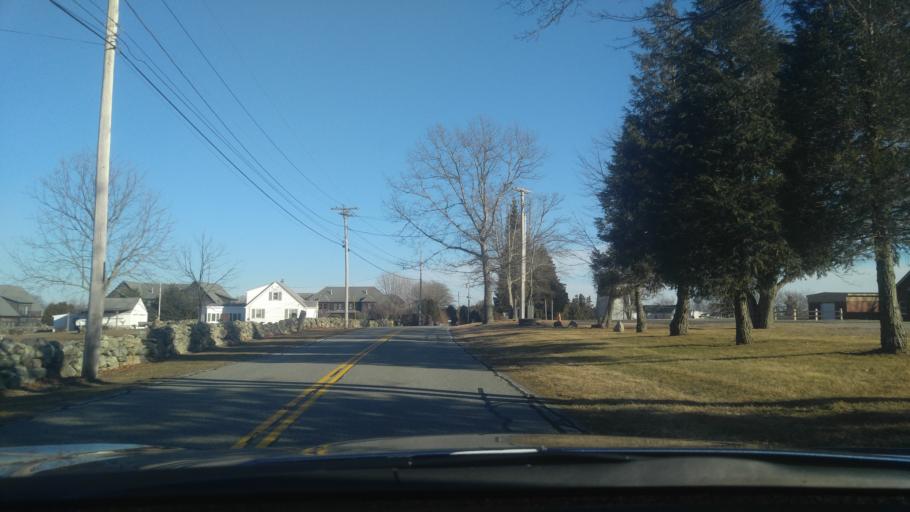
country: US
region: Rhode Island
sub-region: Washington County
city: Narragansett Pier
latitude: 41.4005
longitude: -71.4779
